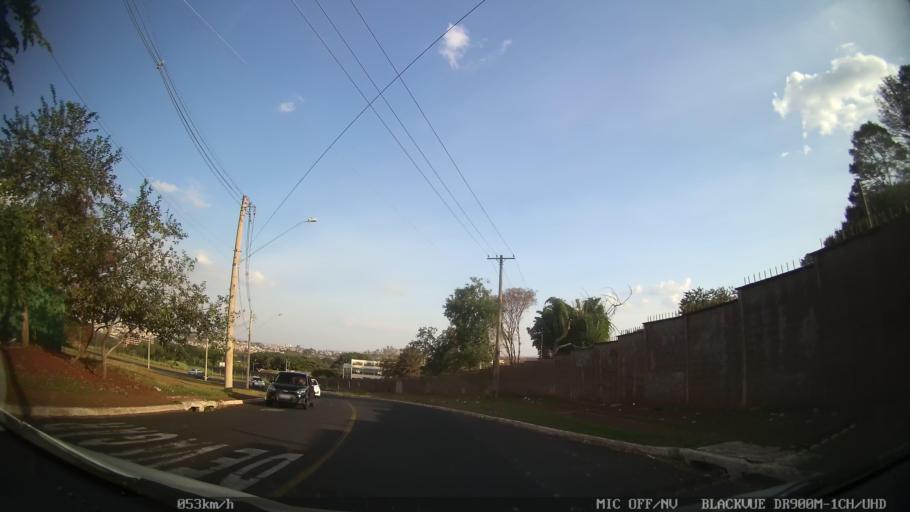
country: BR
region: Sao Paulo
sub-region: Ribeirao Preto
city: Ribeirao Preto
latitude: -21.1680
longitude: -47.8465
